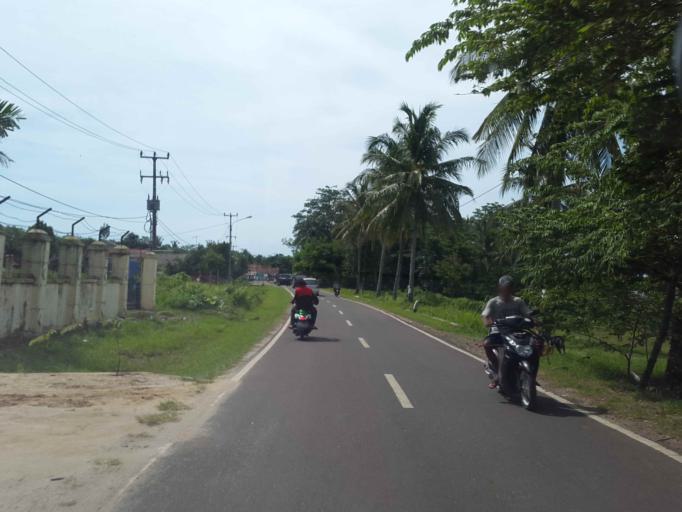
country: ID
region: Banten
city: Citeureup
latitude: -6.5137
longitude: 105.6794
